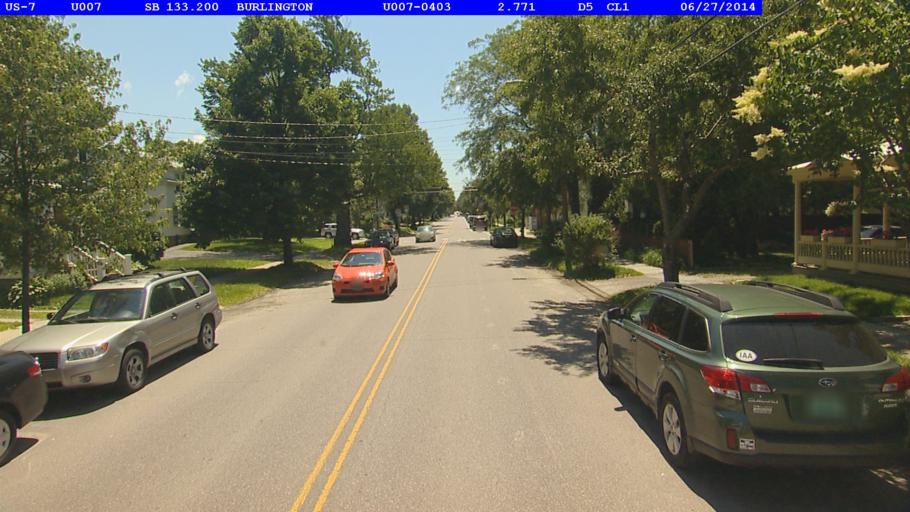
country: US
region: Vermont
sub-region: Chittenden County
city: Burlington
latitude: 44.4855
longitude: -73.2059
